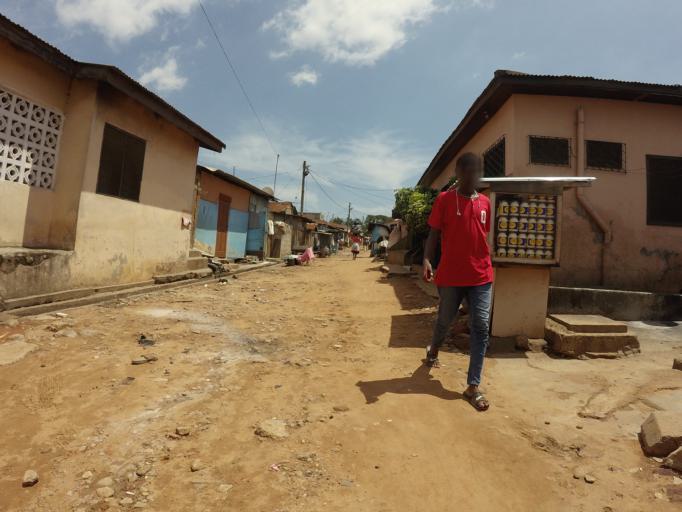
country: GH
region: Greater Accra
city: Accra
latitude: 5.5798
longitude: -0.2015
